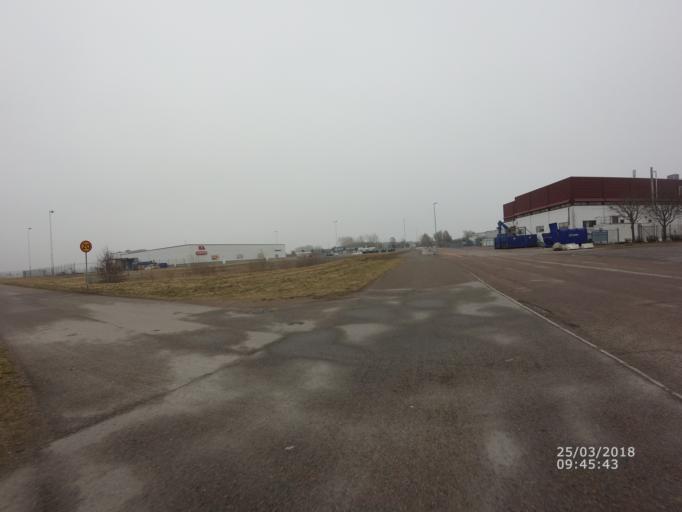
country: SE
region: Skane
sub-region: Hoganas Kommun
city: Hoganas
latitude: 56.1926
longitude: 12.5658
